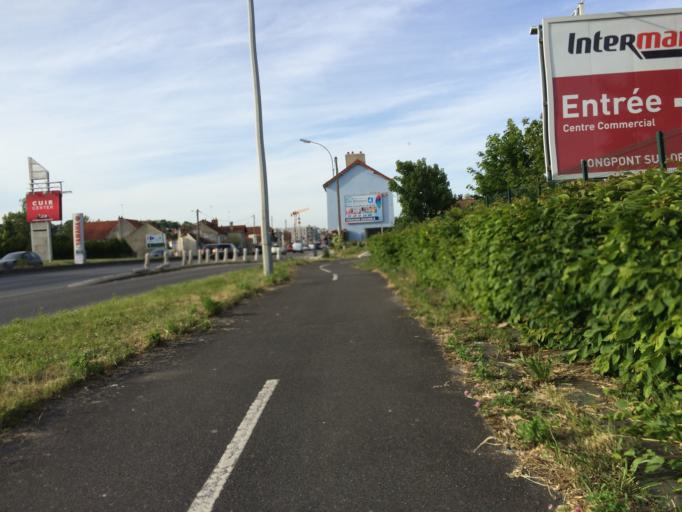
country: FR
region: Ile-de-France
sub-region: Departement de l'Essonne
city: La Ville-du-Bois
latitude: 48.6544
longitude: 2.2740
